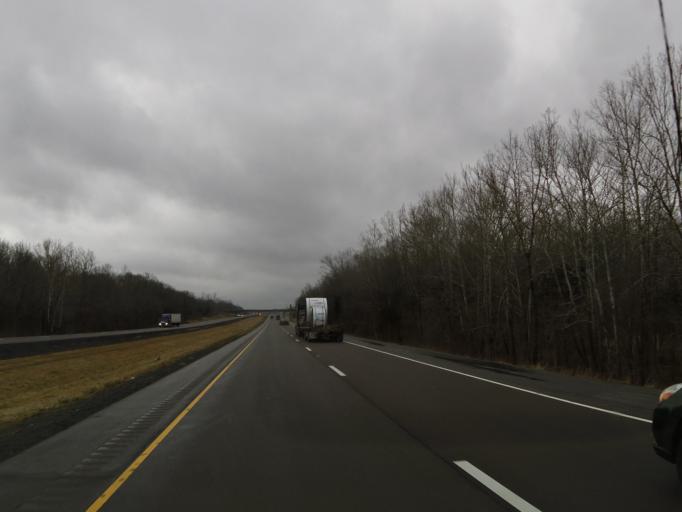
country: US
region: Illinois
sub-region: Williamson County
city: Marion
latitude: 37.6524
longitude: -88.9751
